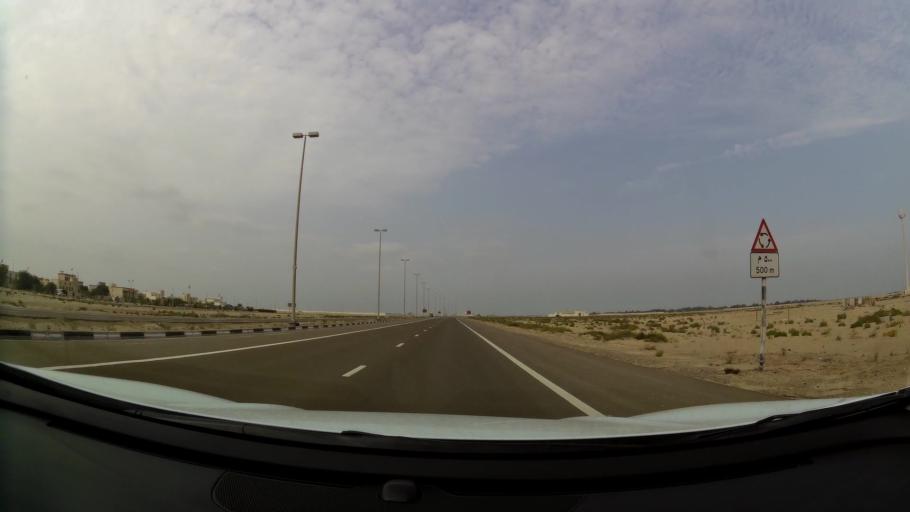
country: AE
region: Abu Dhabi
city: Abu Dhabi
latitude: 24.6387
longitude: 54.6692
